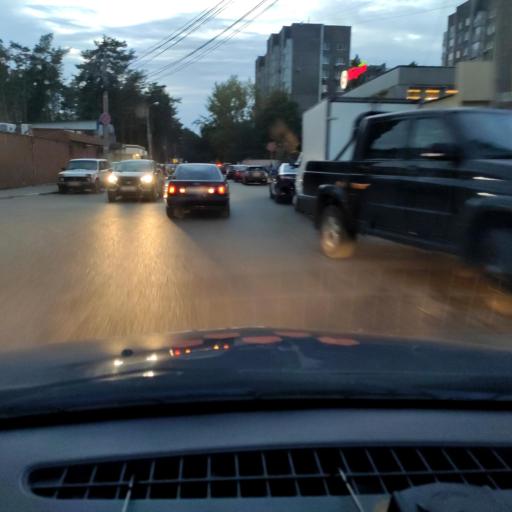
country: RU
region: Voronezj
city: Pridonskoy
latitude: 51.6829
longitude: 39.0847
